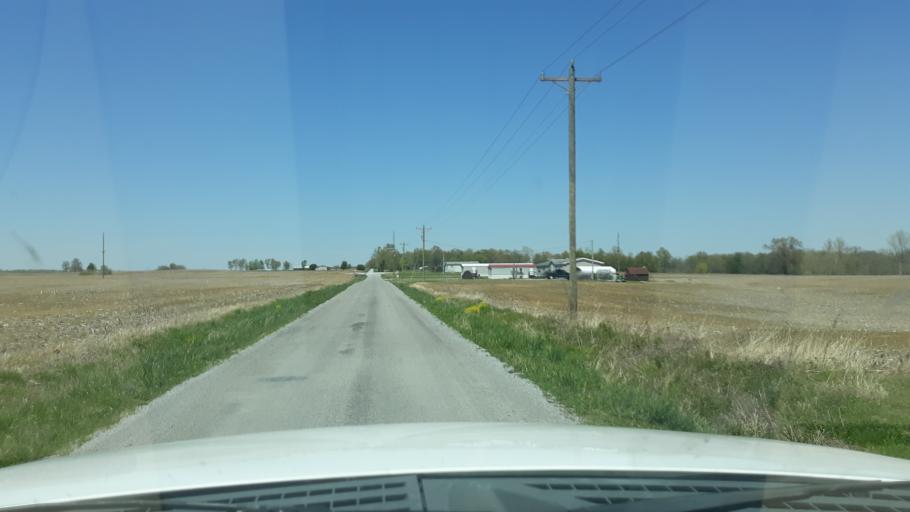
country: US
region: Illinois
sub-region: Saline County
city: Harrisburg
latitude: 37.8748
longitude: -88.6421
